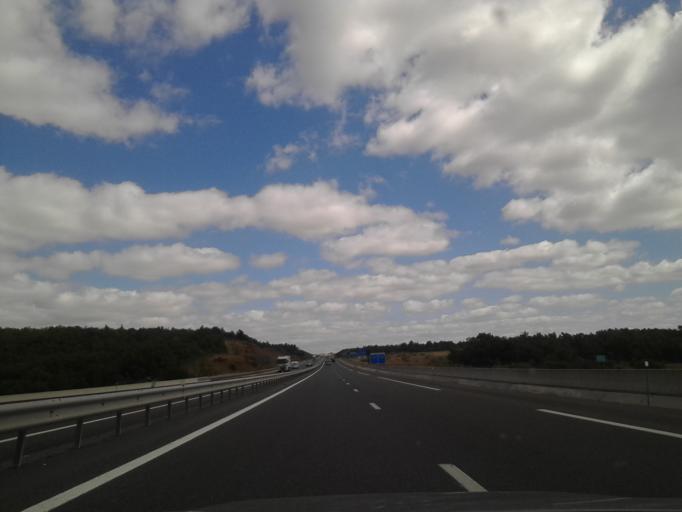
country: FR
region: Midi-Pyrenees
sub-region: Departement de l'Aveyron
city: Creissels
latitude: 44.1563
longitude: 3.0215
